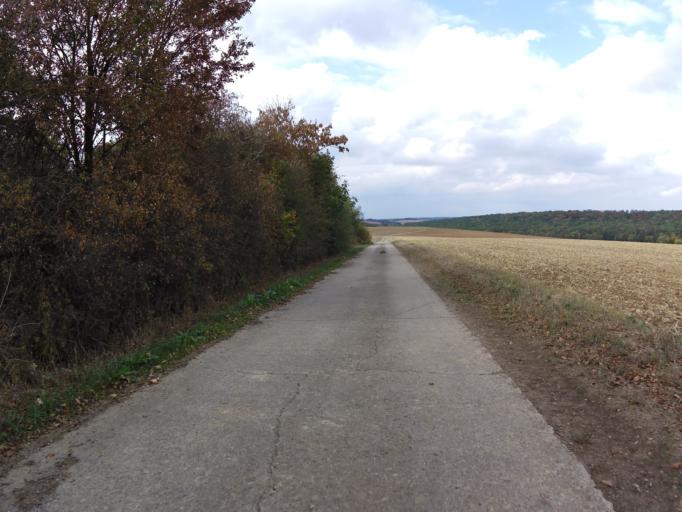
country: DE
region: Bavaria
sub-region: Regierungsbezirk Unterfranken
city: Waldbrunn
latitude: 49.7642
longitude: 9.8162
